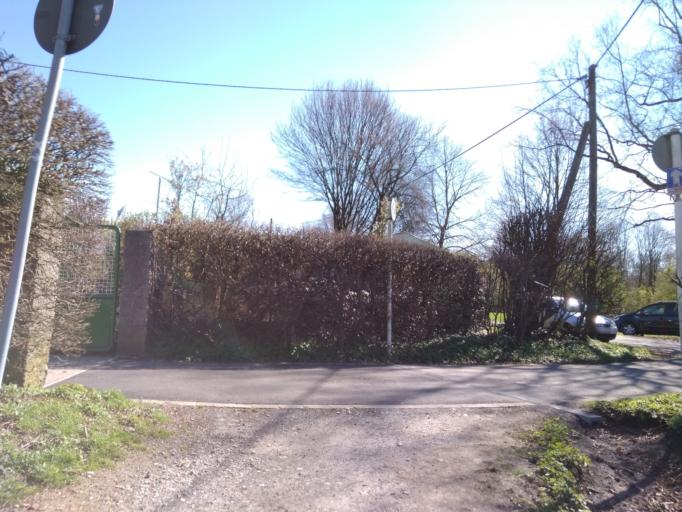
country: DE
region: North Rhine-Westphalia
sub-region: Regierungsbezirk Munster
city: Gladbeck
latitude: 51.6101
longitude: 7.0391
